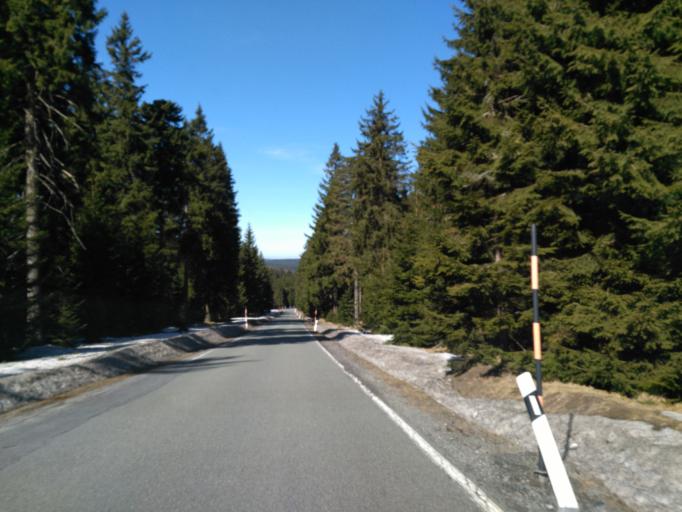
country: DE
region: Saxony
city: Kurort Oberwiesenthal
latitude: 50.4294
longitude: 12.9087
